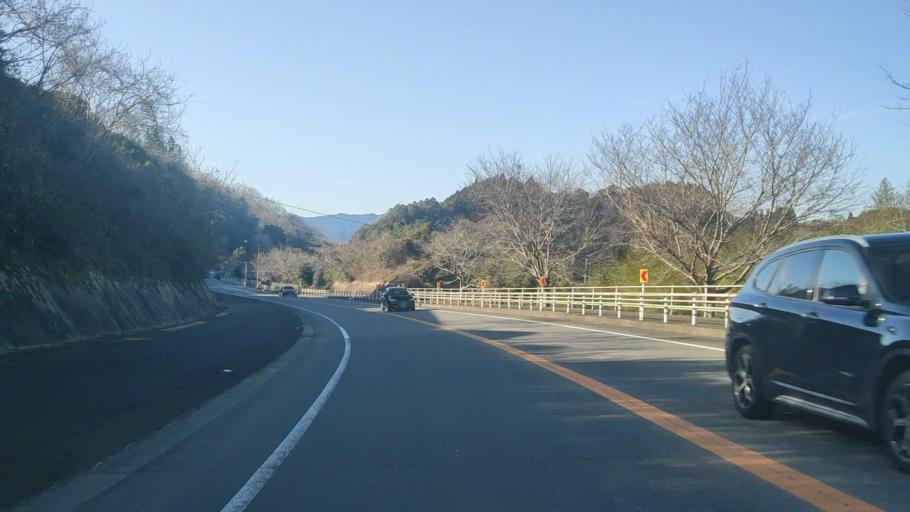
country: JP
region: Oita
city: Usuki
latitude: 33.0606
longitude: 131.6720
